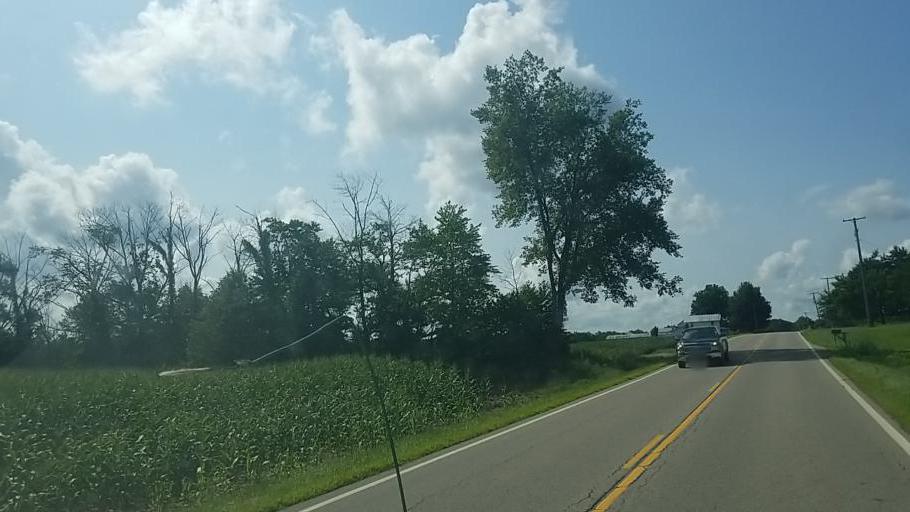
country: US
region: Ohio
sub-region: Ashland County
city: Ashland
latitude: 40.7631
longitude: -82.3069
